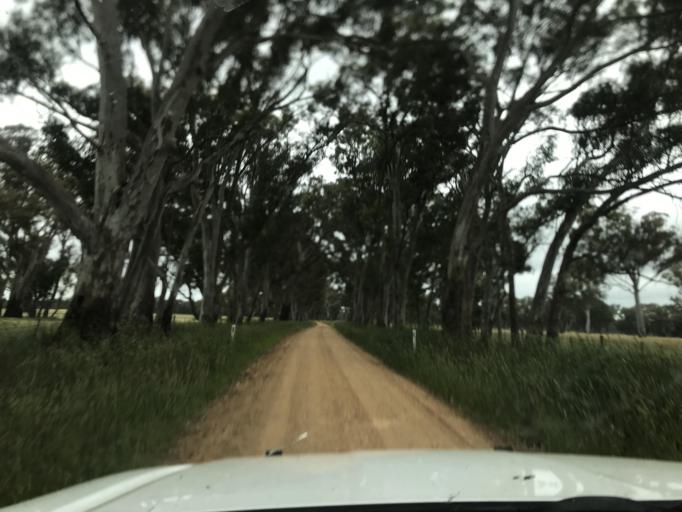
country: AU
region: South Australia
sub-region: Wattle Range
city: Penola
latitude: -37.2705
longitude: 140.9746
